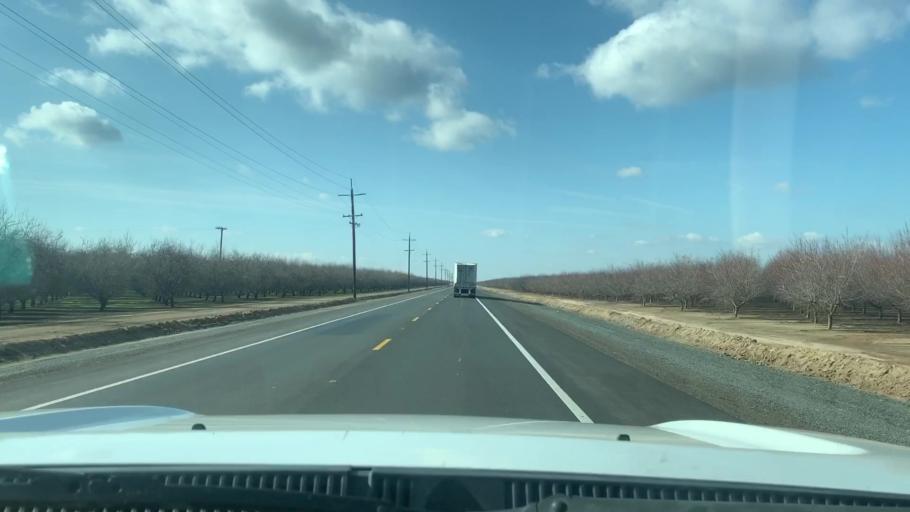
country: US
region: California
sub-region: Kern County
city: McFarland
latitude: 35.6019
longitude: -119.2449
